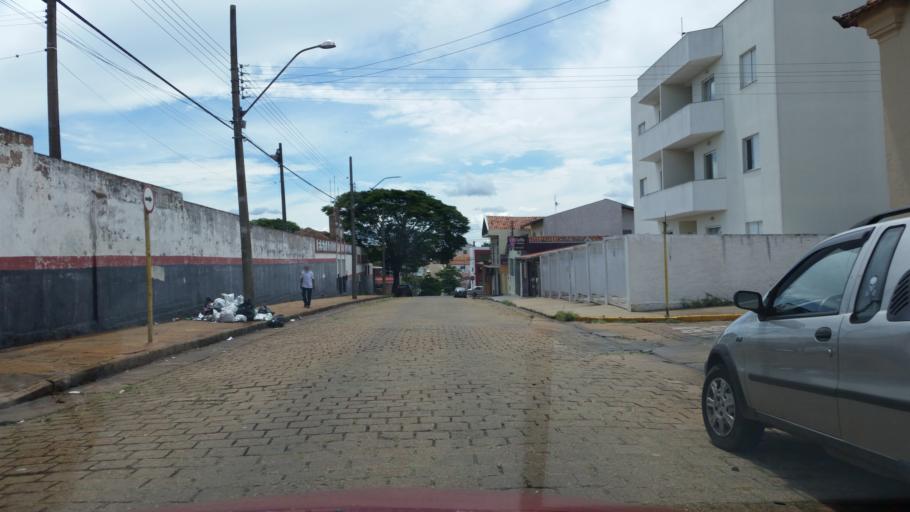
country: BR
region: Sao Paulo
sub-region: Avare
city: Avare
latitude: -23.1034
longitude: -48.9295
